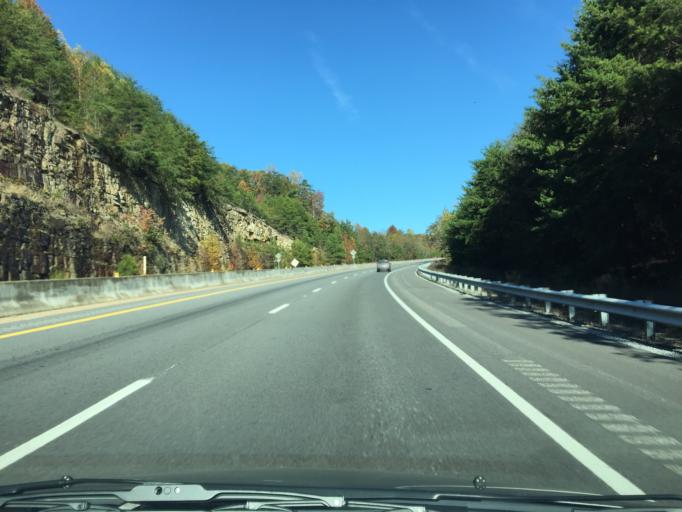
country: US
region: Tennessee
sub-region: Hamilton County
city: Sale Creek
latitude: 35.3265
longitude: -85.1625
